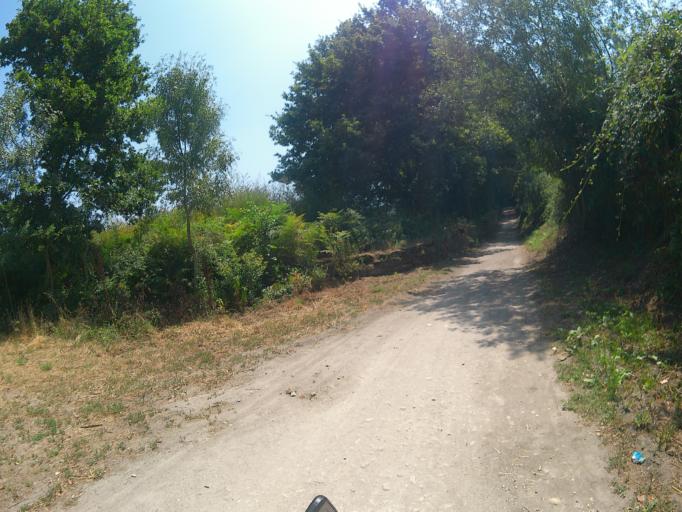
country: PT
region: Viana do Castelo
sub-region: Ponte de Lima
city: Ponte de Lima
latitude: 41.7761
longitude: -8.5707
